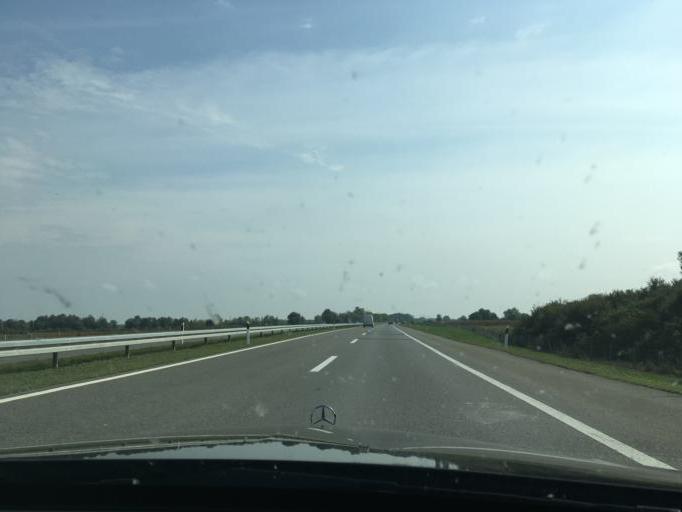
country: HR
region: Vukovarsko-Srijemska
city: Stitar
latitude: 45.1106
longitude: 18.6682
